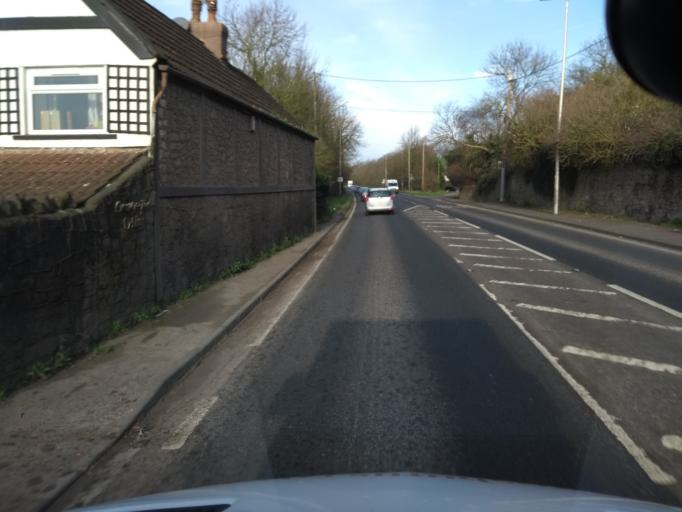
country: GB
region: England
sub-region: North Somerset
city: Bleadon
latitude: 51.3094
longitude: -2.9606
